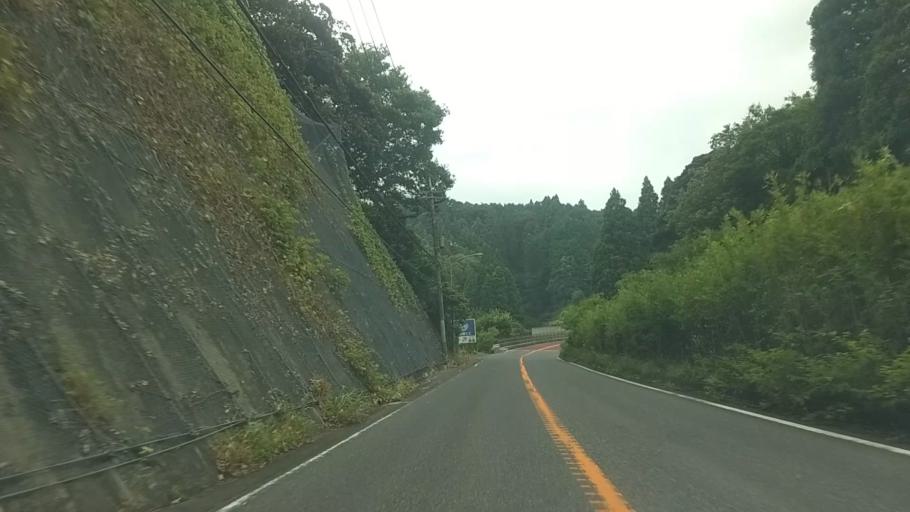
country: JP
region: Chiba
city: Kawaguchi
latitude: 35.2505
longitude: 140.0757
